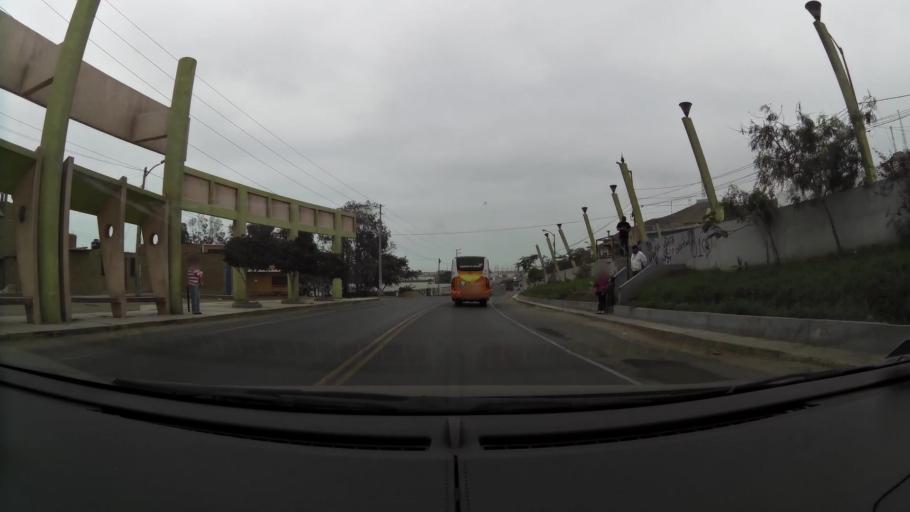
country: PE
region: Ancash
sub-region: Provincia de Santa
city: Coishco
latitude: -9.0191
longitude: -78.6169
